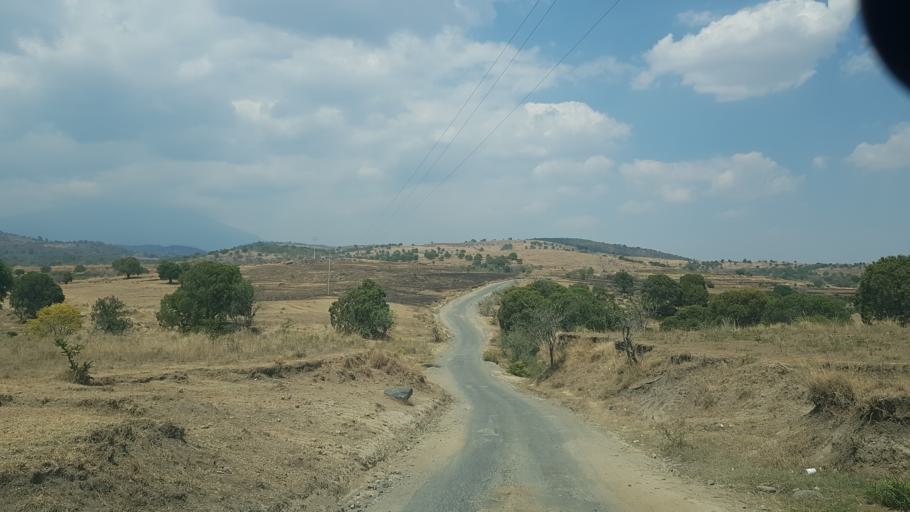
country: MX
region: Puebla
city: San Juan Amecac
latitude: 18.8226
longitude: -98.6232
